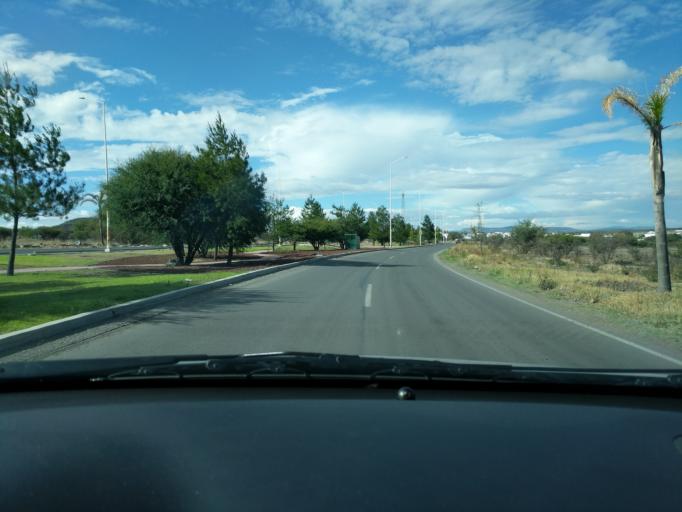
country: MX
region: Queretaro
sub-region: El Marques
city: Paseos del Marques
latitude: 20.5927
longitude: -100.2783
